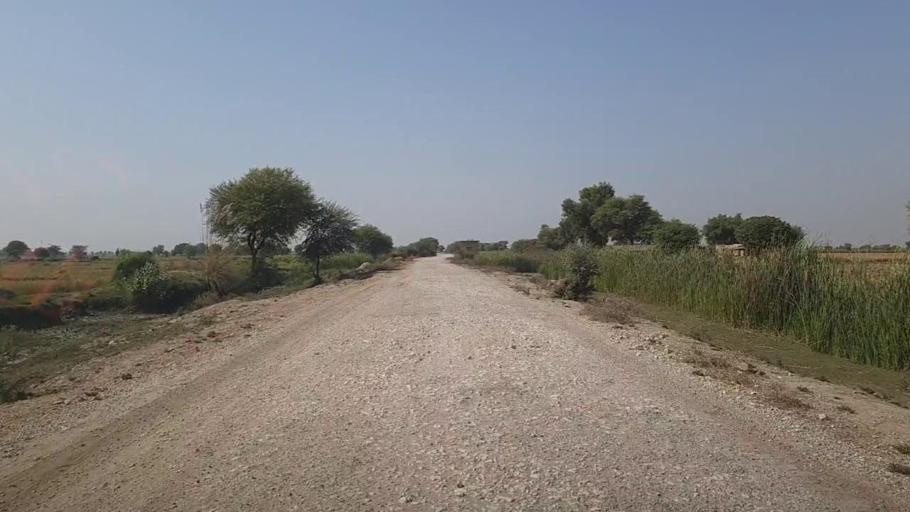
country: PK
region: Sindh
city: Kandhkot
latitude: 28.3927
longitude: 69.2807
